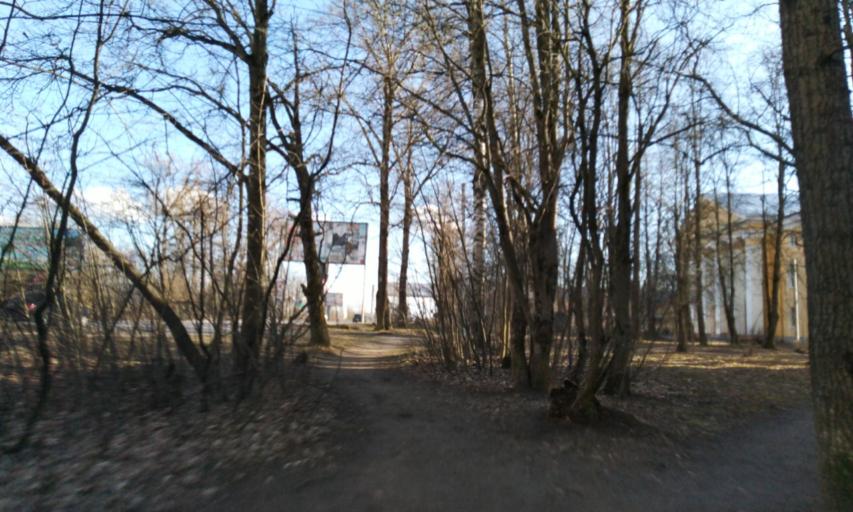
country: RU
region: Leningrad
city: Toksovo
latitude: 60.1098
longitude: 30.5007
